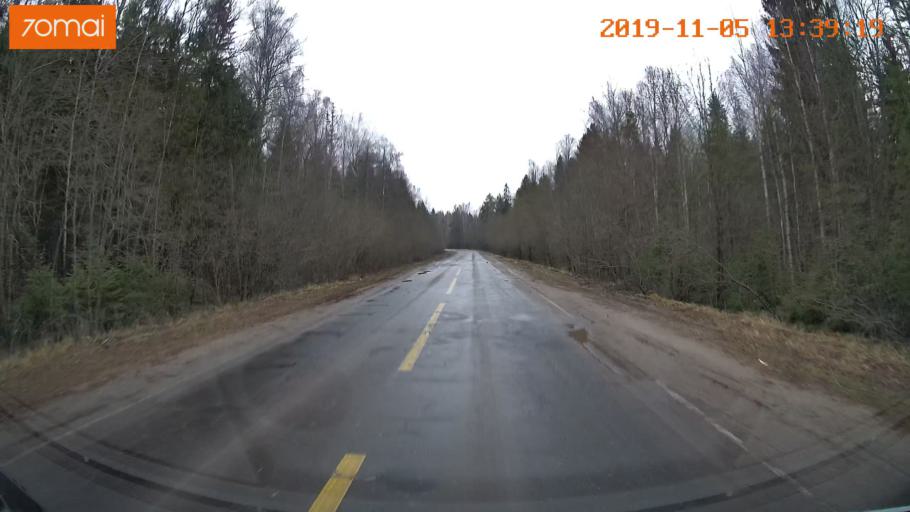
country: RU
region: Ivanovo
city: Shuya
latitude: 56.9386
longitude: 41.3868
